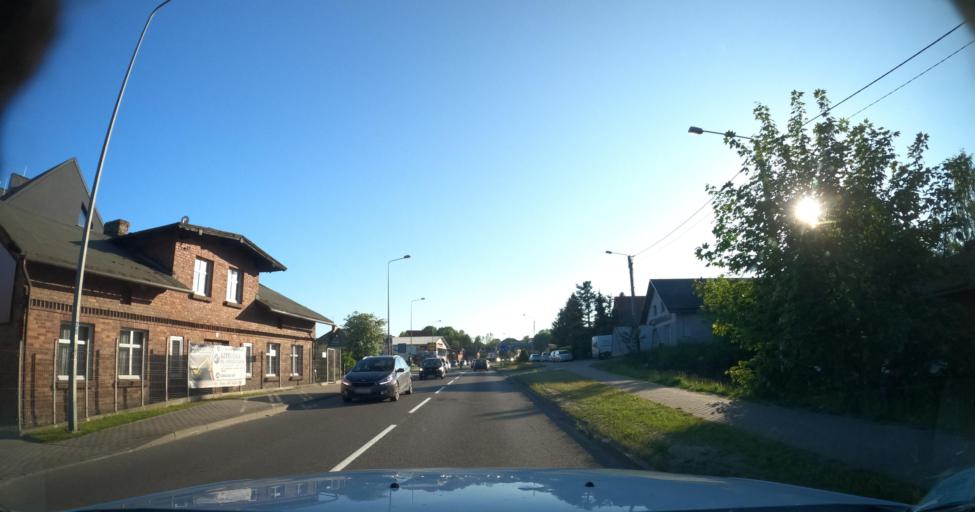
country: PL
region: Pomeranian Voivodeship
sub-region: Powiat kartuski
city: Zukowo
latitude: 54.3408
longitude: 18.3536
